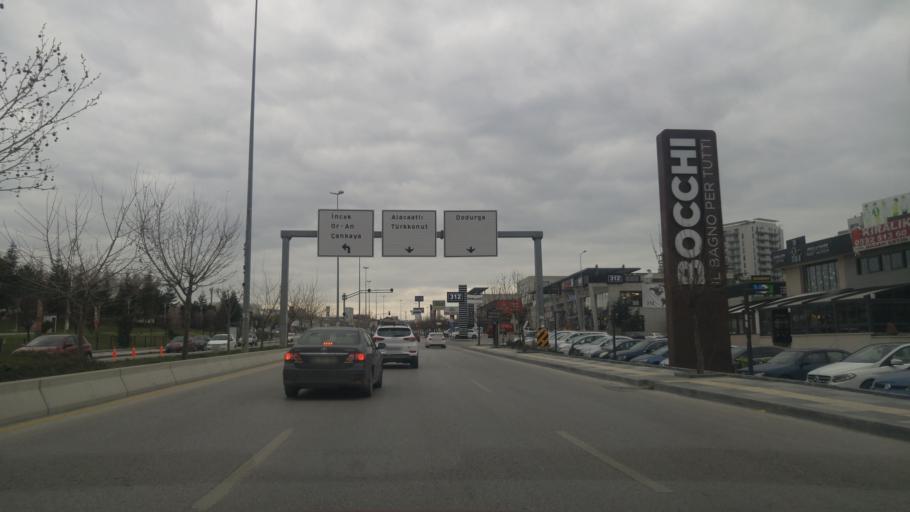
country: TR
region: Ankara
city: Etimesgut
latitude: 39.8695
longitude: 32.6864
